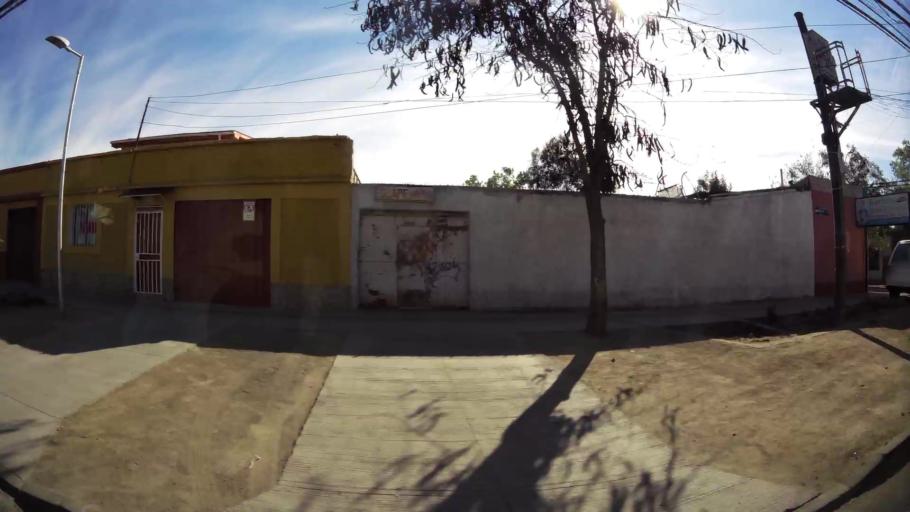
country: CL
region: Santiago Metropolitan
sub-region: Provincia de Santiago
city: Lo Prado
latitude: -33.4677
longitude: -70.6932
